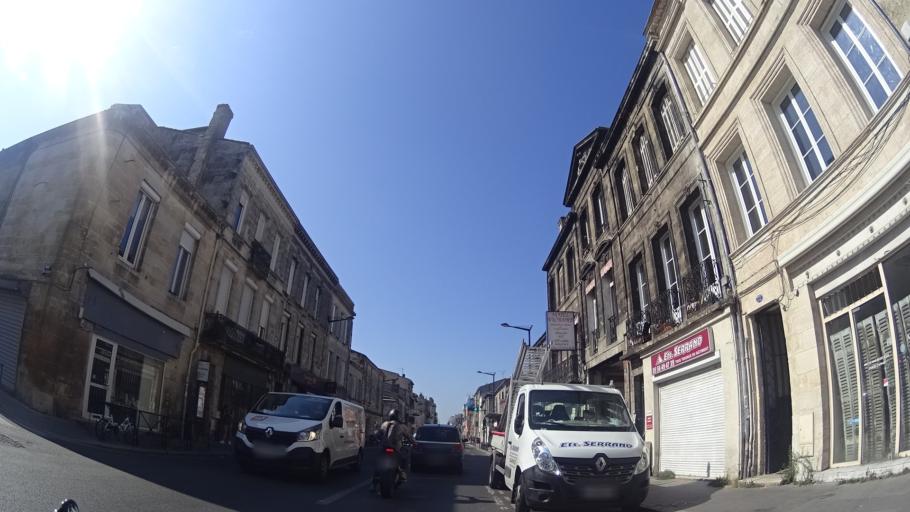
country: FR
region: Aquitaine
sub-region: Departement de la Gironde
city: Bordeaux
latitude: 44.8277
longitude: -0.5725
